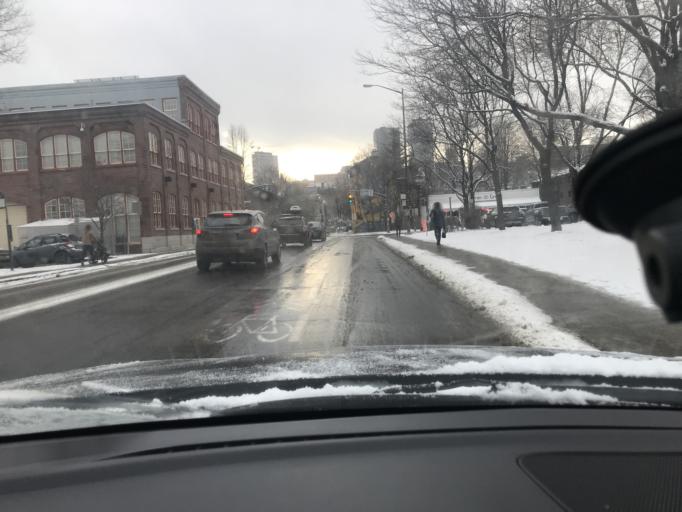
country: CA
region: Quebec
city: Quebec
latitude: 46.8183
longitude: -71.2230
